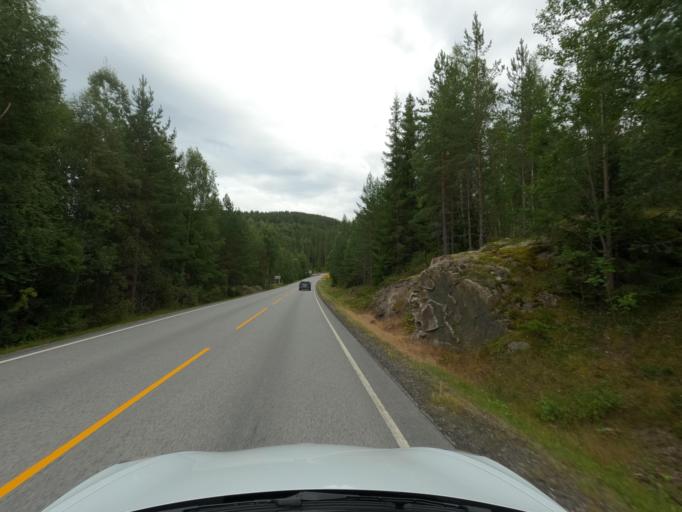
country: NO
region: Telemark
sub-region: Hjartdal
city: Sauland
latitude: 59.6907
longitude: 9.0231
